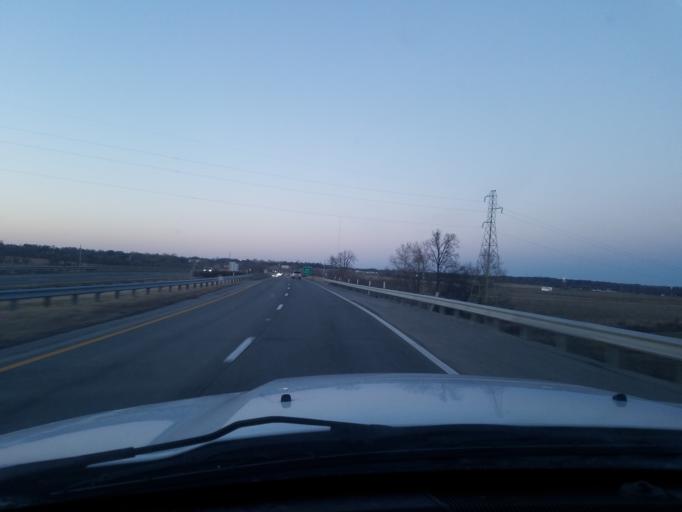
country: US
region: Kentucky
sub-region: Henderson County
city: Henderson
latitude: 37.8387
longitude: -87.5645
